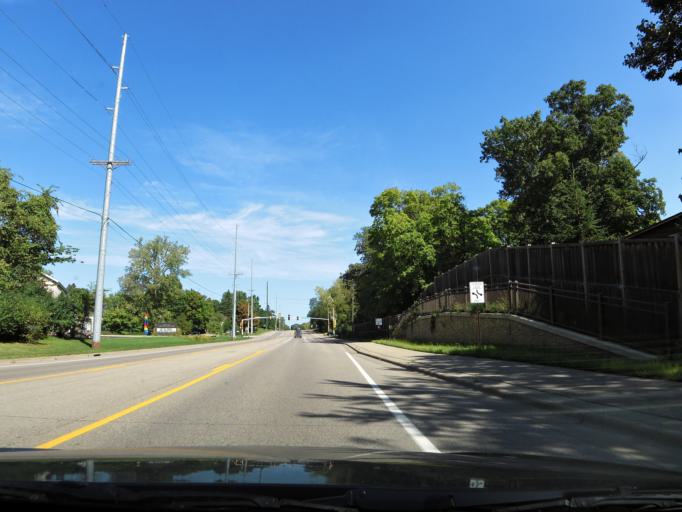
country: US
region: Minnesota
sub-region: Hennepin County
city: Minnetonka
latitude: 44.9263
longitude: -93.5029
